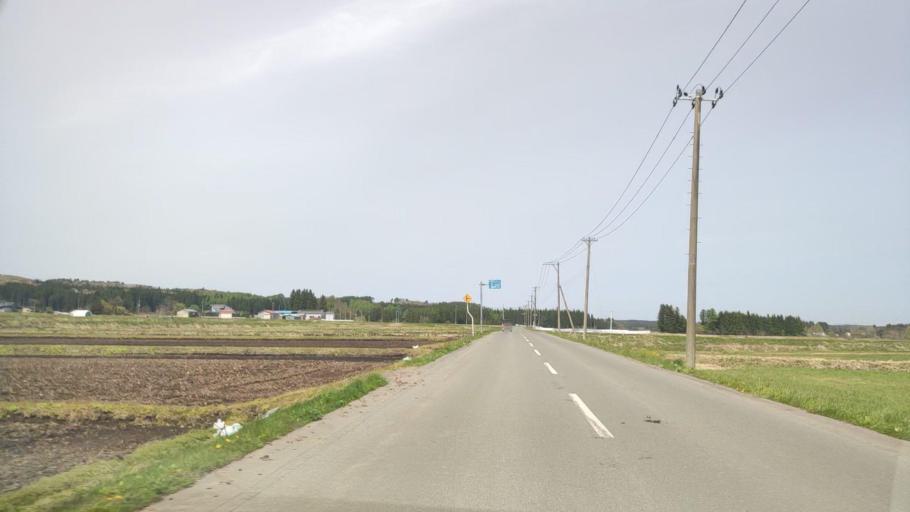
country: JP
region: Aomori
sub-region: Misawa Shi
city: Inuotose
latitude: 40.7605
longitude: 141.1195
